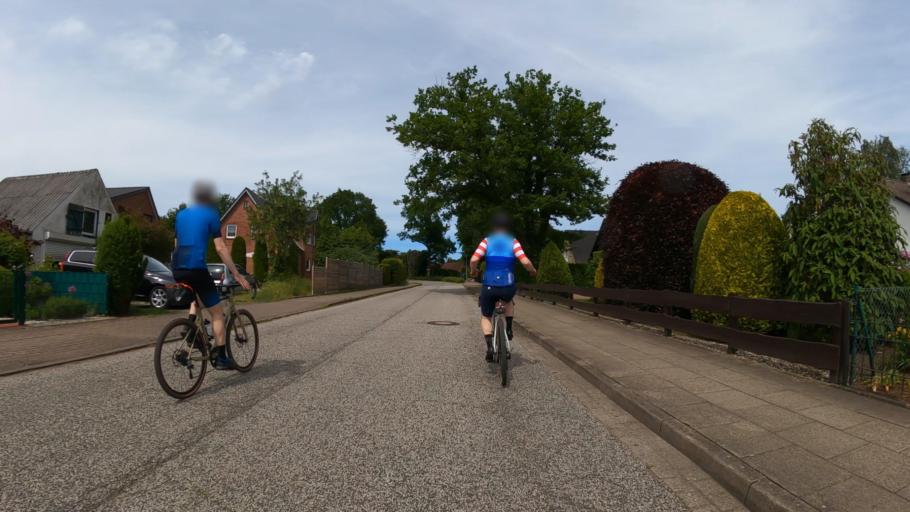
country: DE
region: Schleswig-Holstein
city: Henstedt-Ulzburg
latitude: 53.7567
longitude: 10.0068
